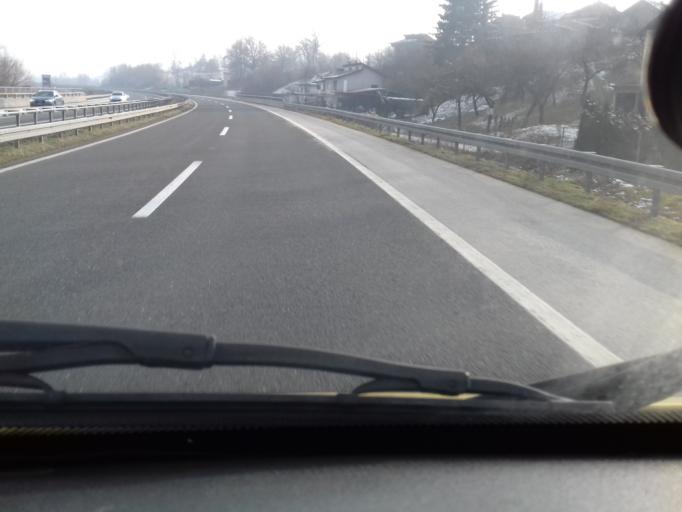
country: BA
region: Federation of Bosnia and Herzegovina
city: Dobrinje
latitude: 44.0364
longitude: 18.1221
